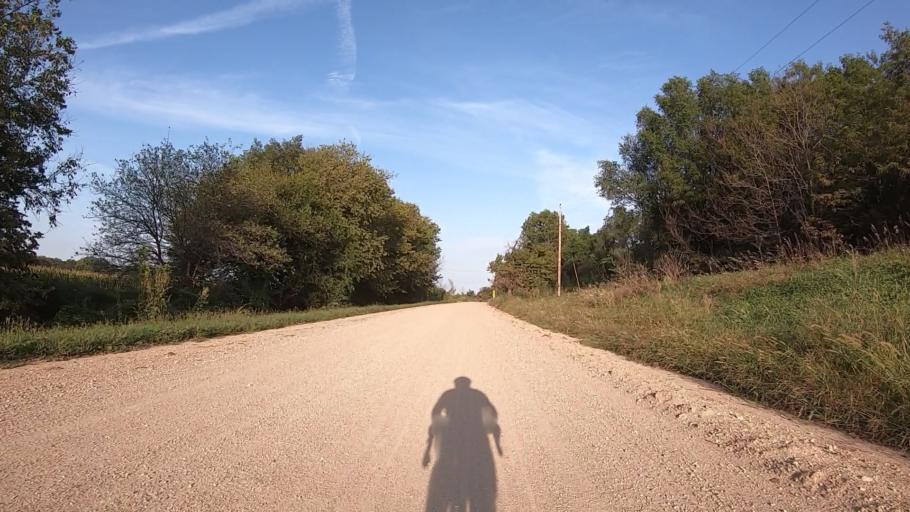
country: US
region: Kansas
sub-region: Marshall County
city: Blue Rapids
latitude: 39.7219
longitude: -96.7746
